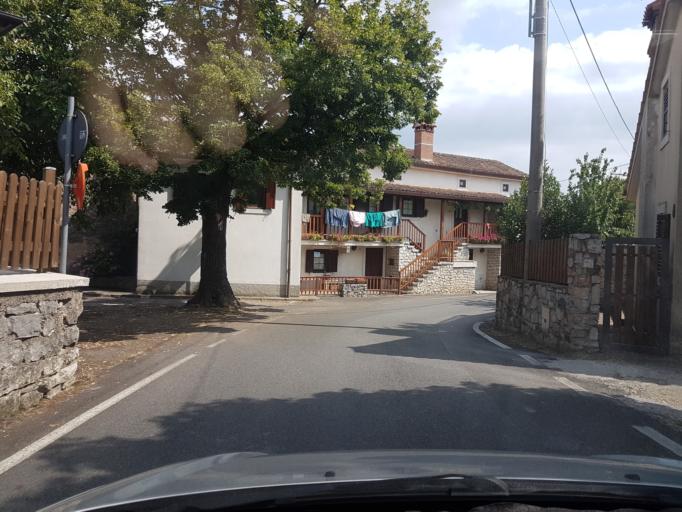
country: IT
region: Friuli Venezia Giulia
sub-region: Provincia di Trieste
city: Villa Opicina
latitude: 45.7068
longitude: 13.7662
